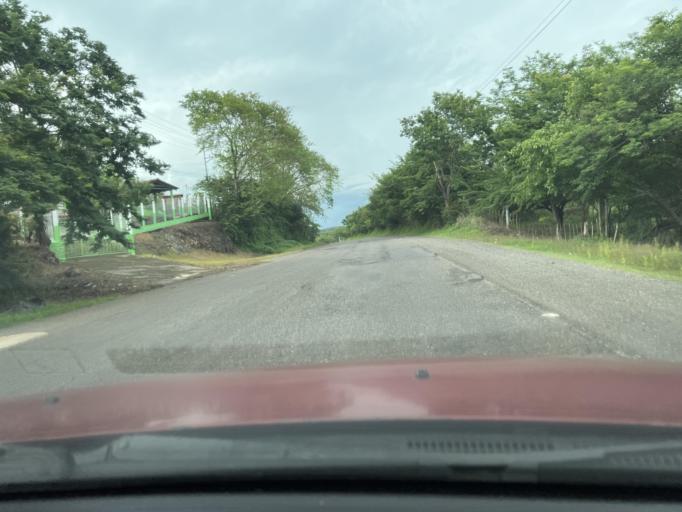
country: SV
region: La Union
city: San Alejo
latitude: 13.4029
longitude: -87.8946
